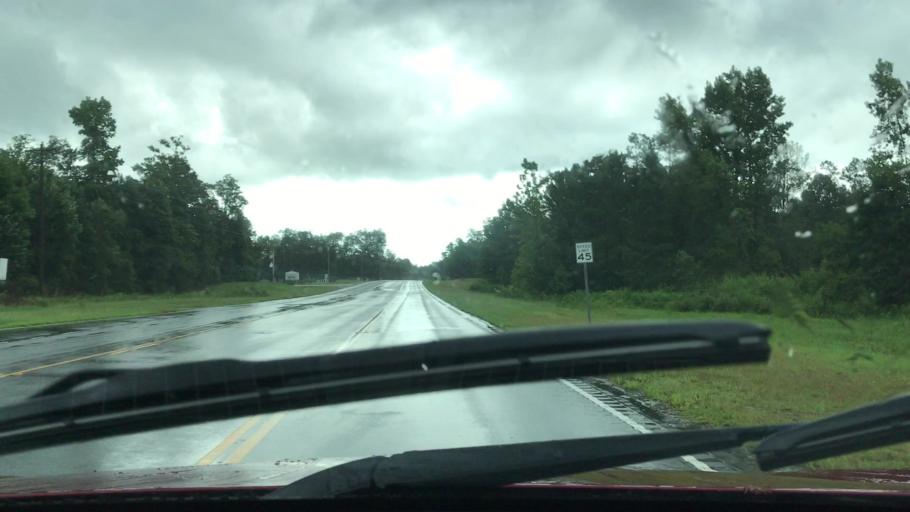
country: US
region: South Carolina
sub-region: Horry County
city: Loris
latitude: 33.9043
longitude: -78.8547
